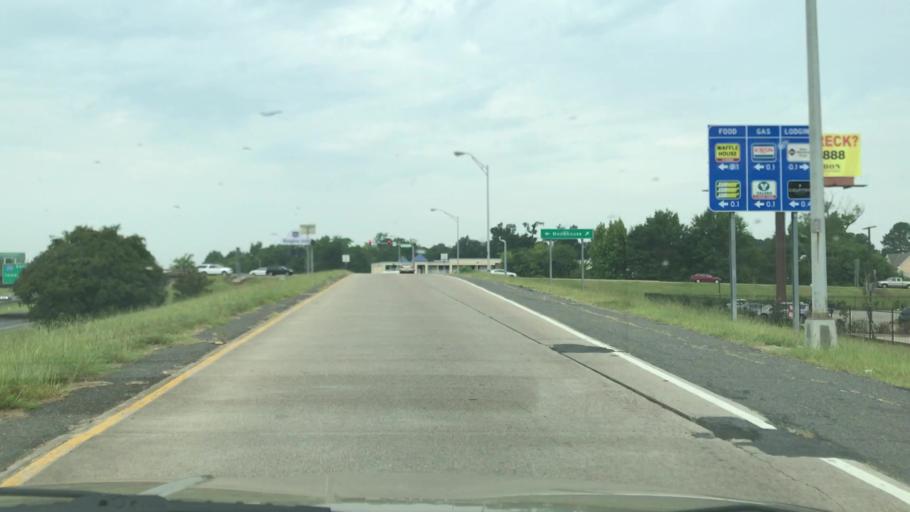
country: US
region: Louisiana
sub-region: Caddo Parish
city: Shreveport
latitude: 32.4625
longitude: -93.8261
